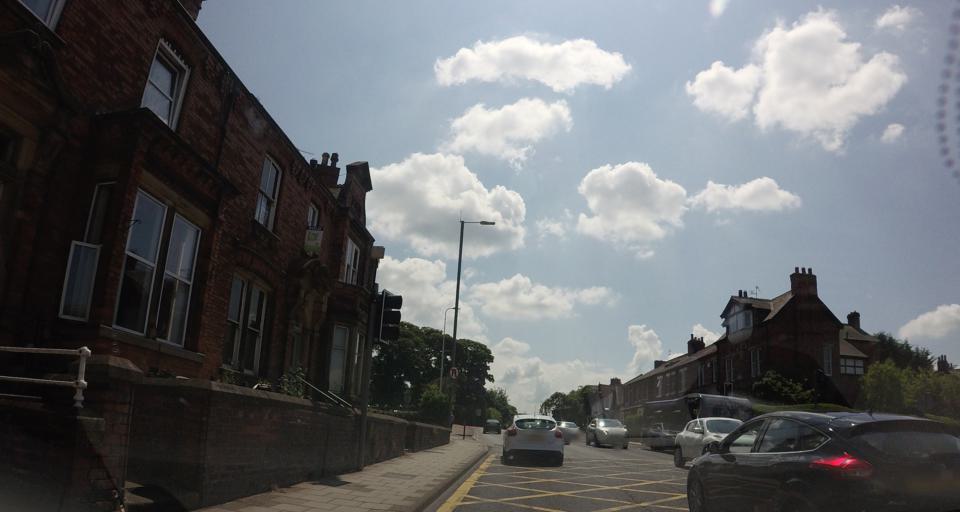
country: GB
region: England
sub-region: Cumbria
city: Carlisle
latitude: 54.9049
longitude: -2.9372
